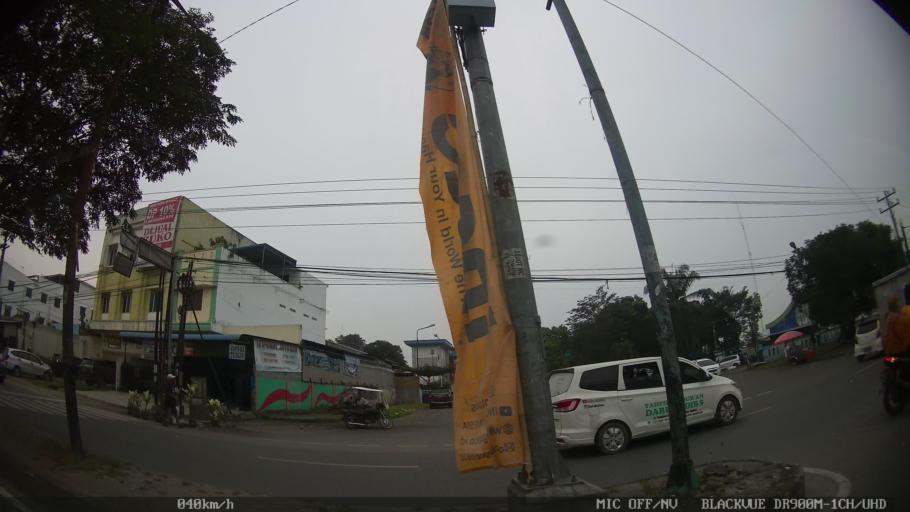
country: ID
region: North Sumatra
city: Deli Tua
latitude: 3.5389
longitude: 98.7175
